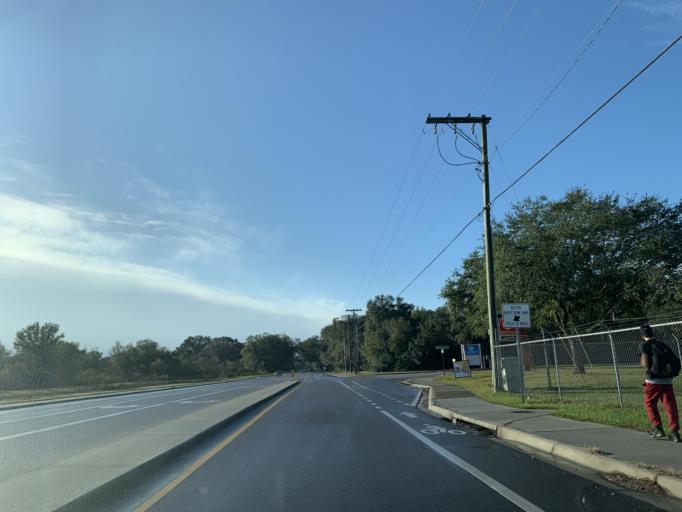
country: US
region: Florida
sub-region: Hillsborough County
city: Mango
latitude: 27.9806
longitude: -82.3188
